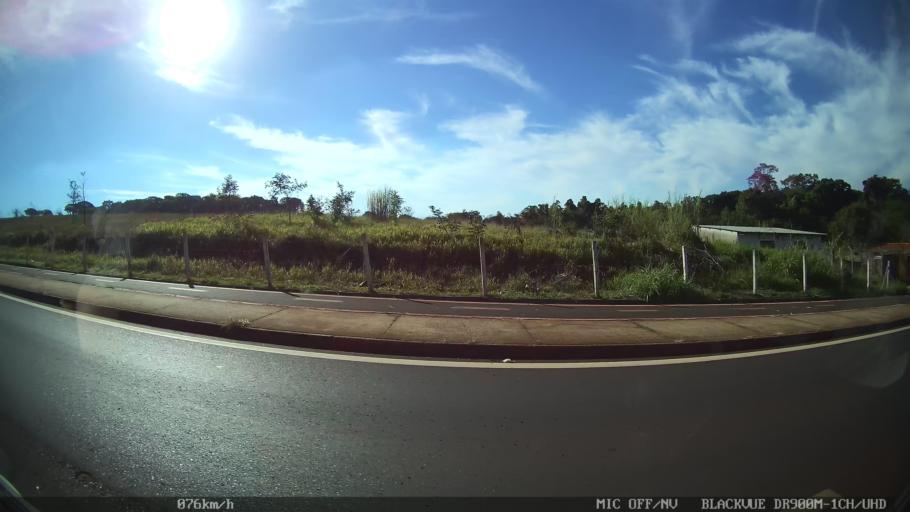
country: BR
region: Sao Paulo
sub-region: Araraquara
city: Araraquara
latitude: -21.7907
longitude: -48.1496
